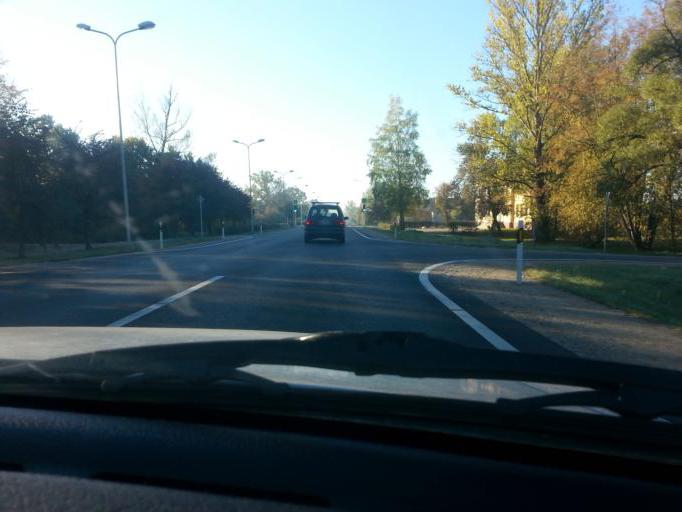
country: LT
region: Siauliu apskritis
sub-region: Joniskis
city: Joniskis
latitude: 56.4122
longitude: 23.6827
